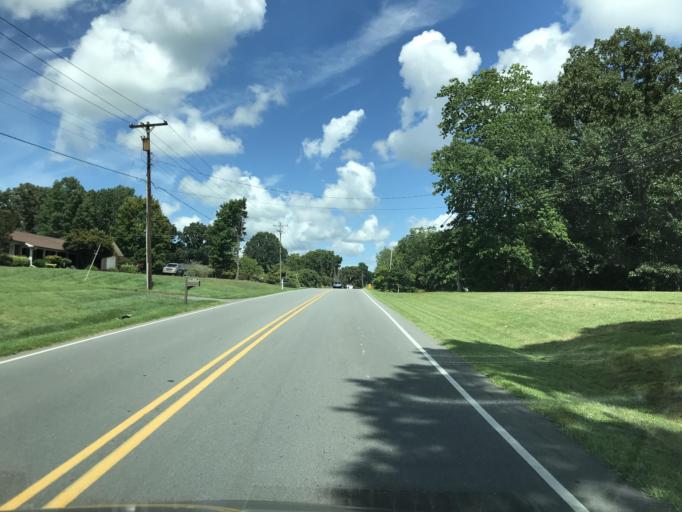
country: US
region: North Carolina
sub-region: Lincoln County
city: Pumpkin Center
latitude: 35.5002
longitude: -81.1875
